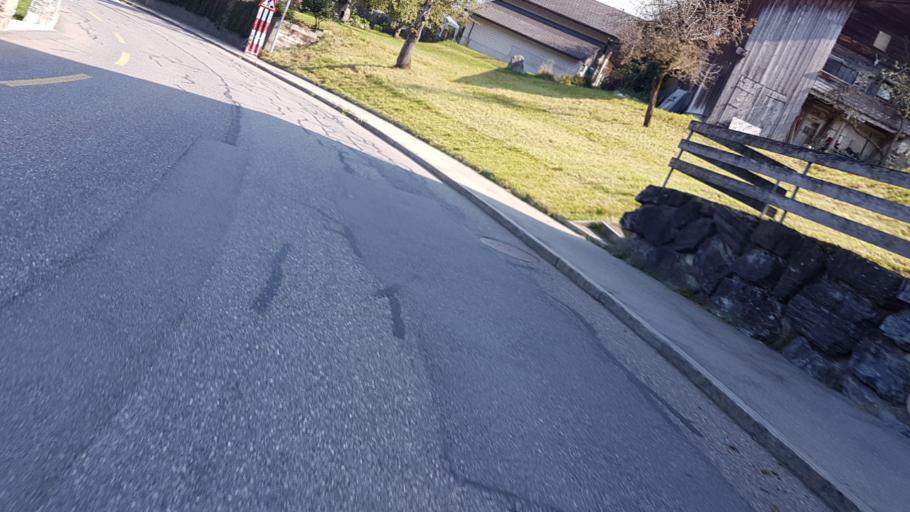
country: CH
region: Bern
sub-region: Frutigen-Niedersimmental District
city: Spiez
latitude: 46.6723
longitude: 7.6826
